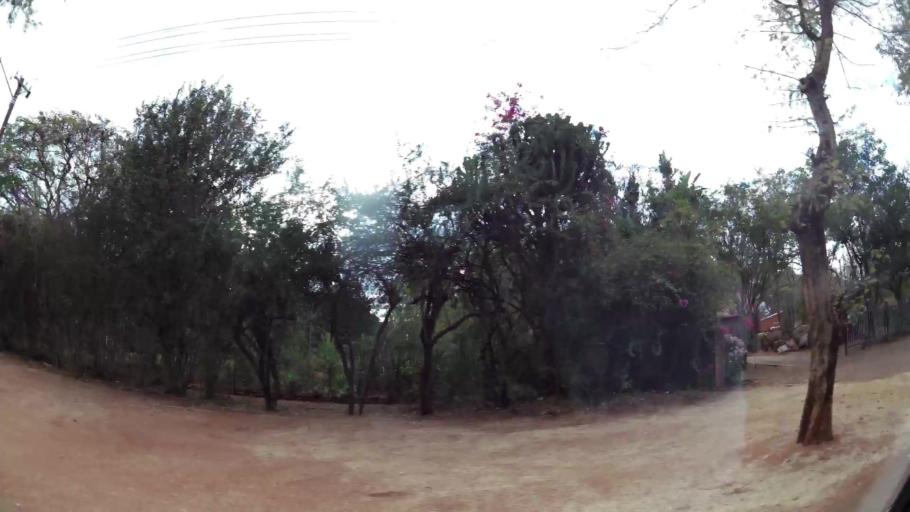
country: ZA
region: Limpopo
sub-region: Waterberg District Municipality
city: Modimolle
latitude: -24.5114
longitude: 28.7144
